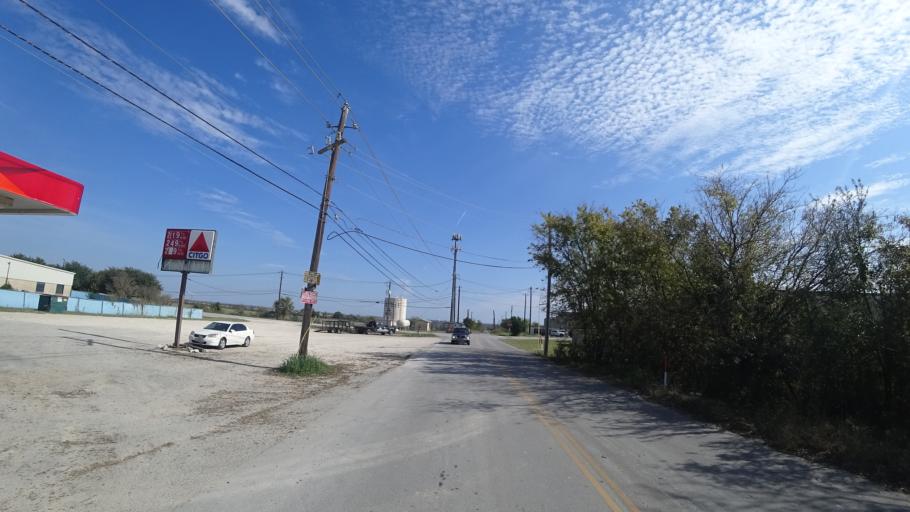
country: US
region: Texas
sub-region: Travis County
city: Pflugerville
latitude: 30.4060
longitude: -97.6290
